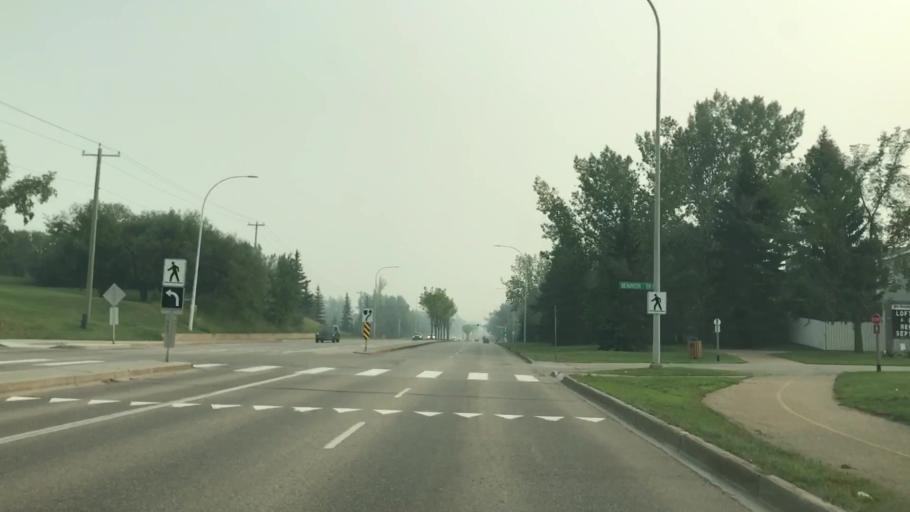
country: CA
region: Alberta
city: Sherwood Park
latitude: 53.5317
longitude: -113.3202
